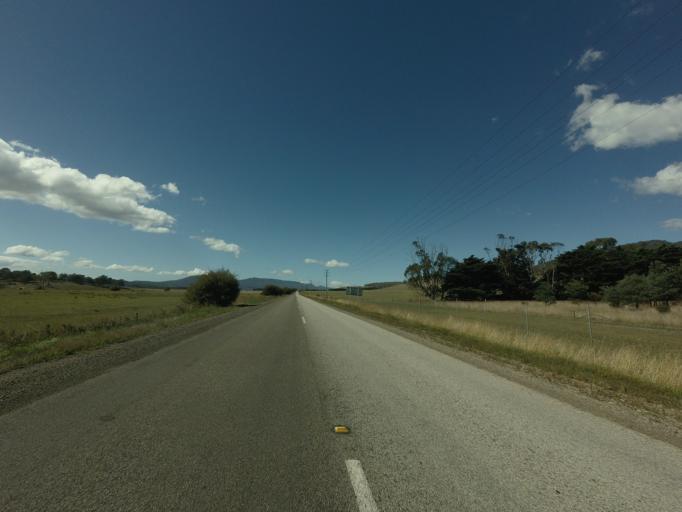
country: AU
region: Tasmania
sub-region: Break O'Day
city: St Helens
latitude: -41.6278
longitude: 147.9902
